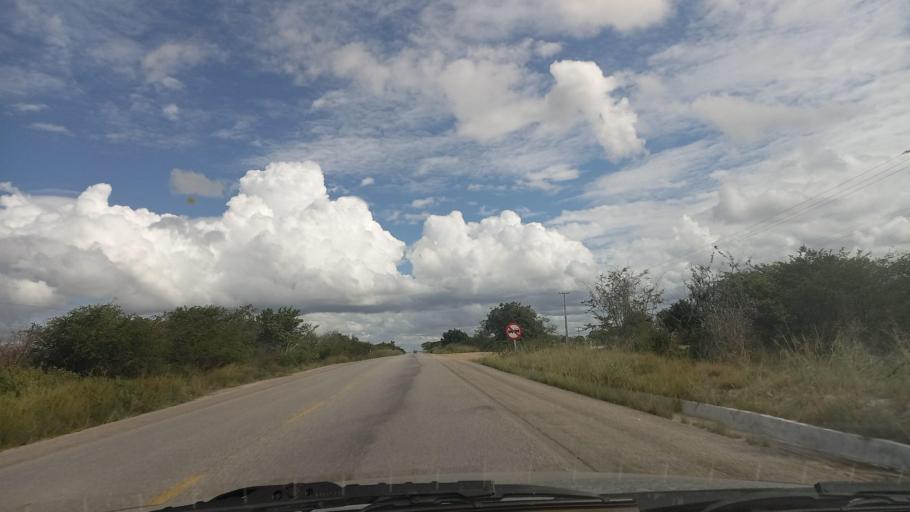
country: BR
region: Pernambuco
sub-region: Cachoeirinha
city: Cachoeirinha
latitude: -8.4405
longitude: -36.2056
